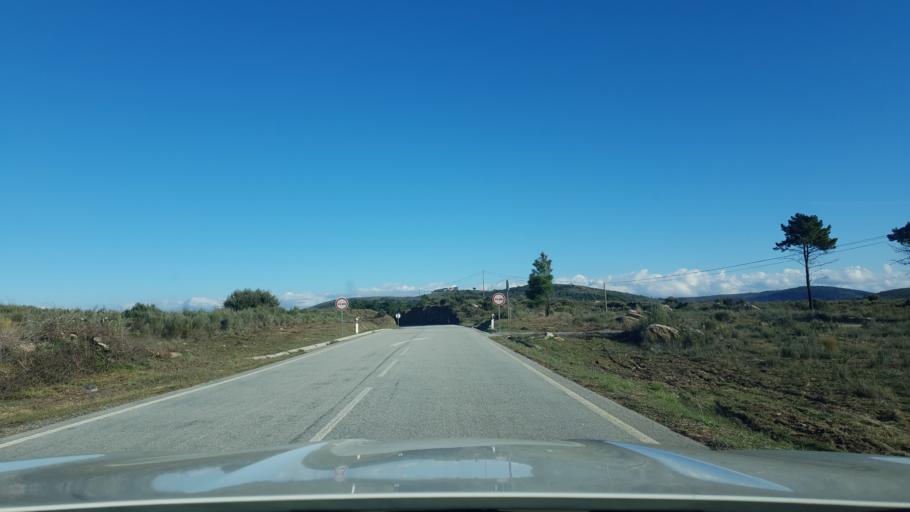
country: PT
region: Braganca
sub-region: Freixo de Espada A Cinta
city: Freixo de Espada a Cinta
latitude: 41.1839
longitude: -6.8457
